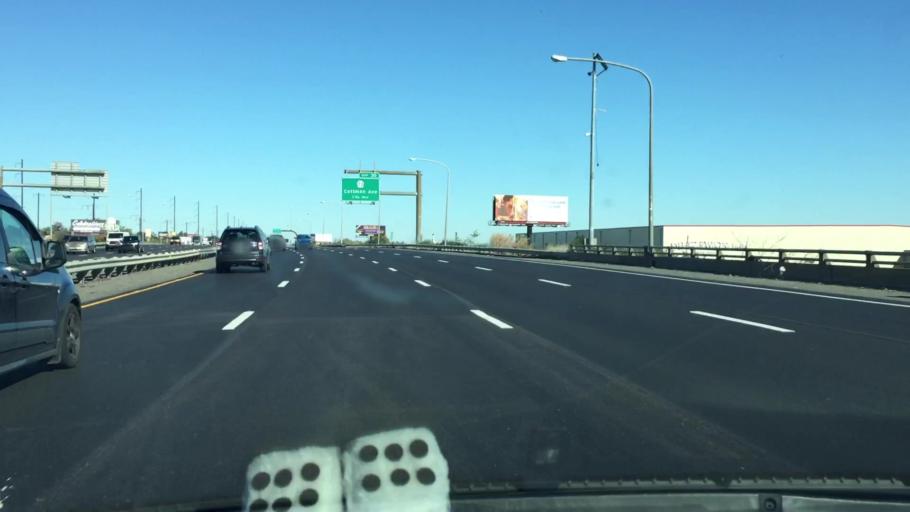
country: US
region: New Jersey
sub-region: Burlington County
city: Palmyra
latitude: 40.0103
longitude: -75.0630
